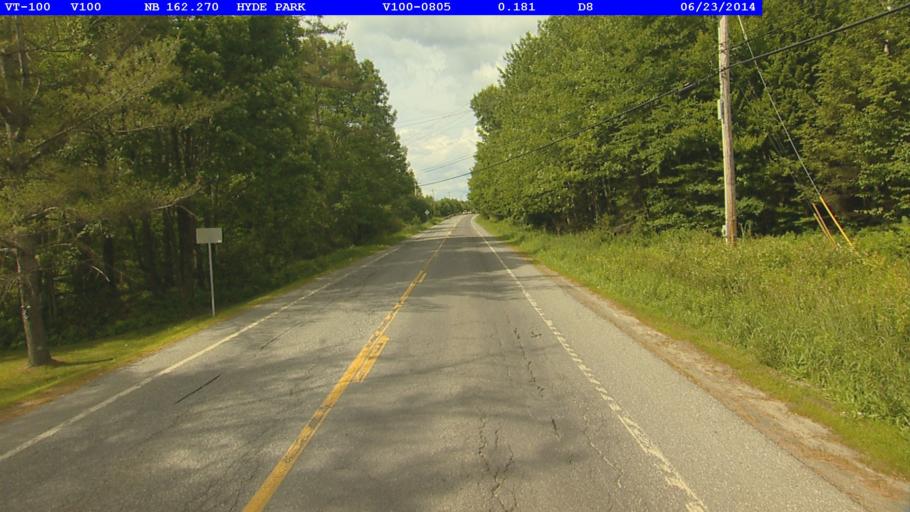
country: US
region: Vermont
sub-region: Lamoille County
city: Hyde Park
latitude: 44.6000
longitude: -72.6154
